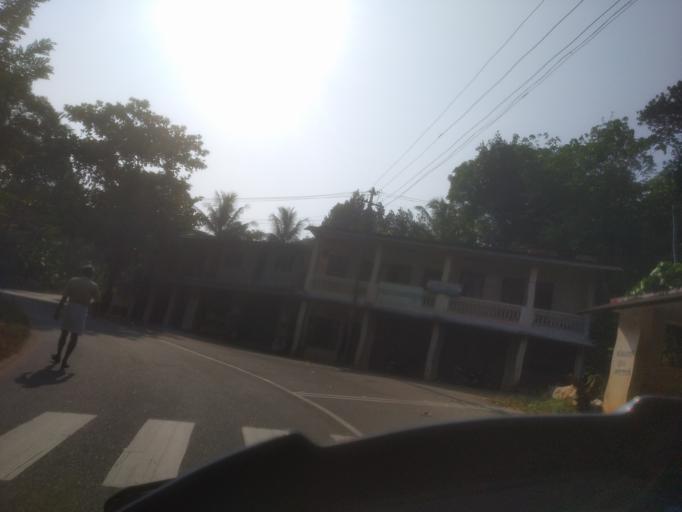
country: IN
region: Kerala
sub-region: Ernakulam
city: Piravam
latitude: 9.8692
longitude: 76.5395
